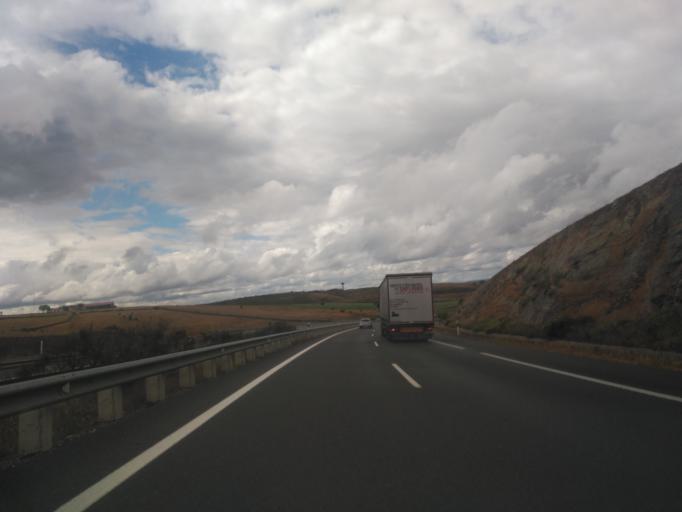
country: ES
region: Castille and Leon
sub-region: Provincia de Salamanca
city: Aldeatejada
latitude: 40.9473
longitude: -5.7068
